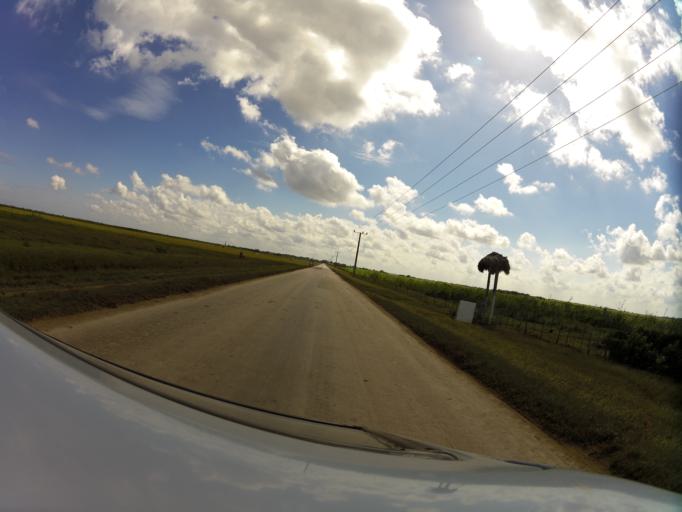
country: CU
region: Las Tunas
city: Jesus Menendez
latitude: 21.2179
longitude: -76.4177
